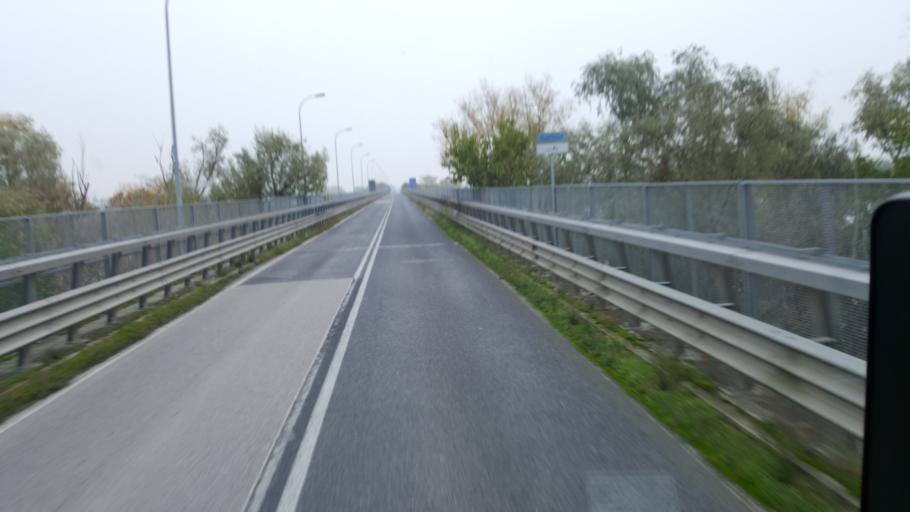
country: IT
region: Veneto
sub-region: Provincia di Rovigo
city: Ficarolo
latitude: 44.9454
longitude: 11.4232
